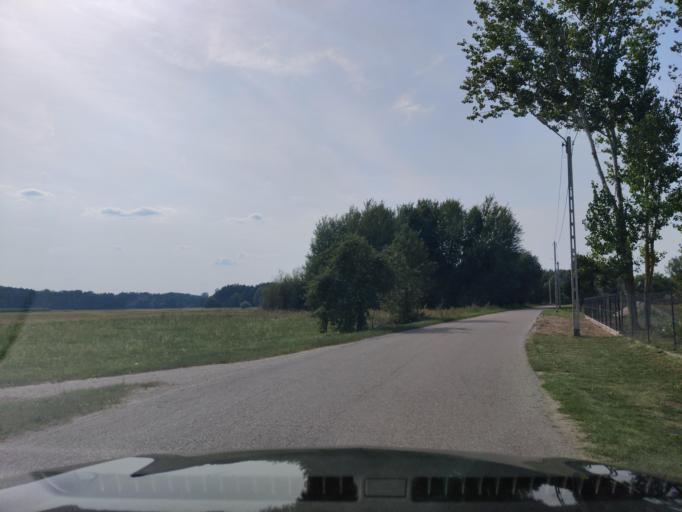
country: PL
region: Masovian Voivodeship
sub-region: Powiat wyszkowski
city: Rzasnik
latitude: 52.7407
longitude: 21.3271
